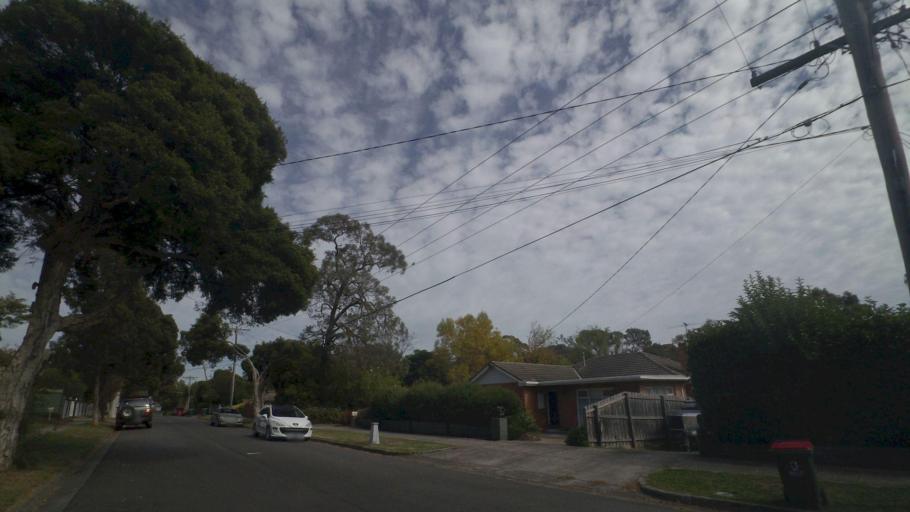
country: AU
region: Victoria
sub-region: Whitehorse
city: Forest Hill
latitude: -37.8352
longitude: 145.1616
